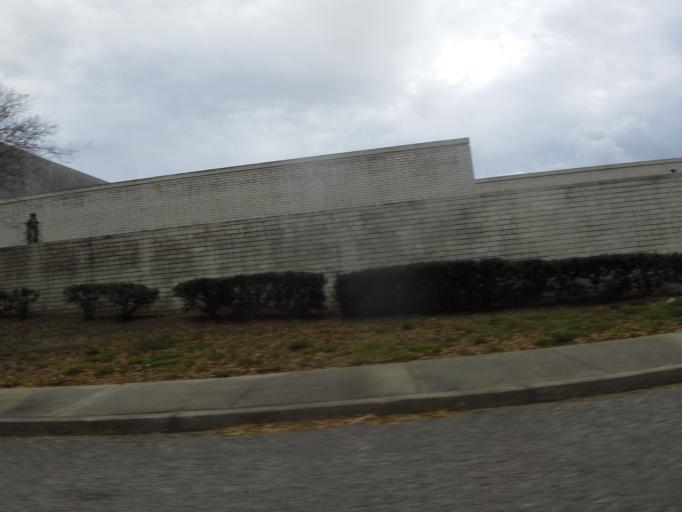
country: US
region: Florida
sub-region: Duval County
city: Jacksonville
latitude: 30.3239
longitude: -81.5529
